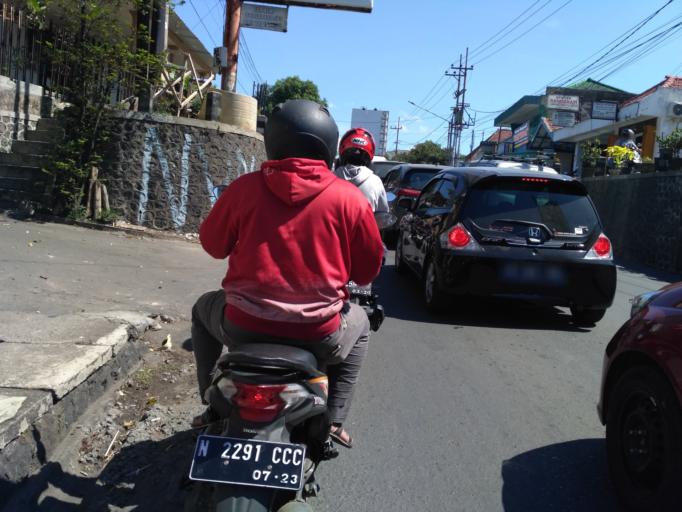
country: ID
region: East Java
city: Malang
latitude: -7.9795
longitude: 112.6505
